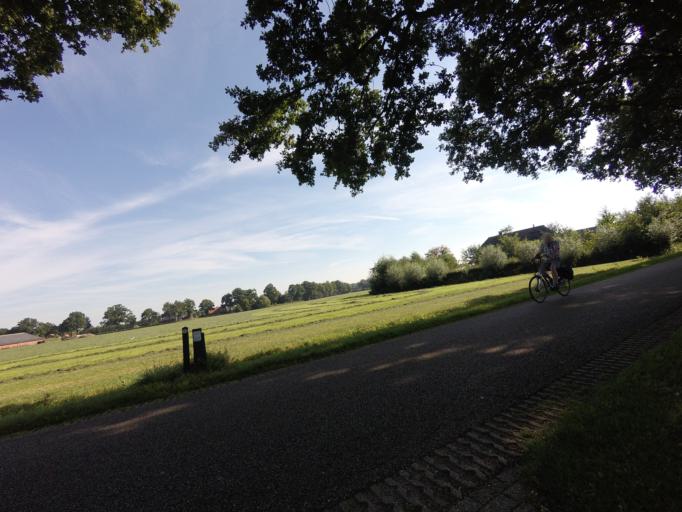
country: NL
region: Gelderland
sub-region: Oost Gelre
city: Lichtenvoorde
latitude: 52.0044
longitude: 6.5036
